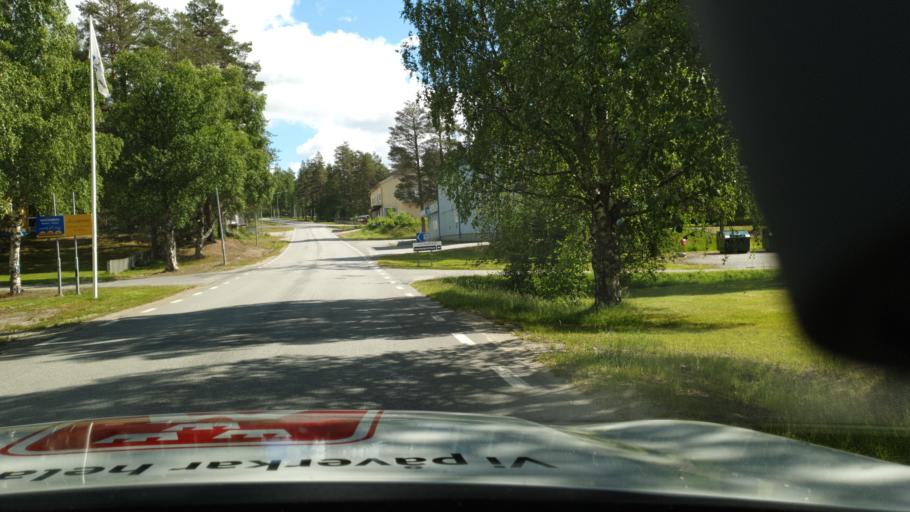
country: SE
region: Vaesterbotten
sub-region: Mala Kommun
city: Mala
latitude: 65.0607
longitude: 18.5749
